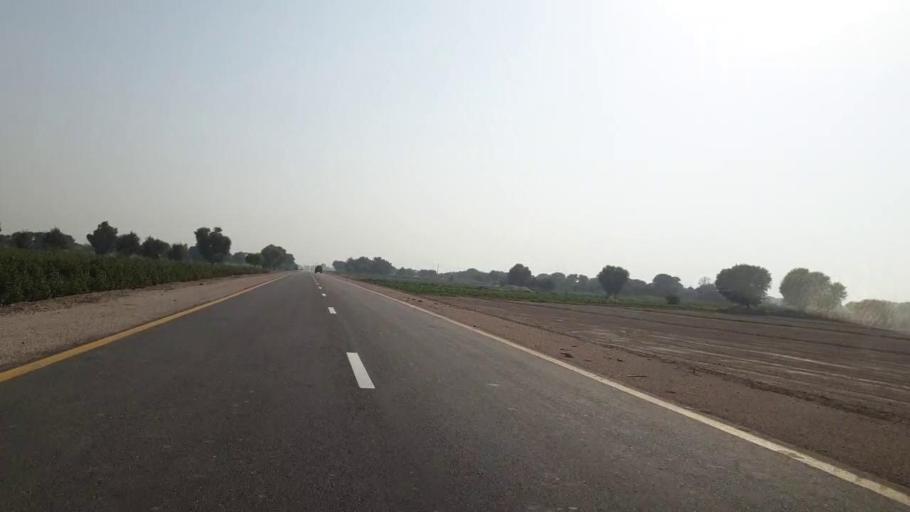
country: PK
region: Sindh
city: Bhan
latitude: 26.5231
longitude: 67.7885
